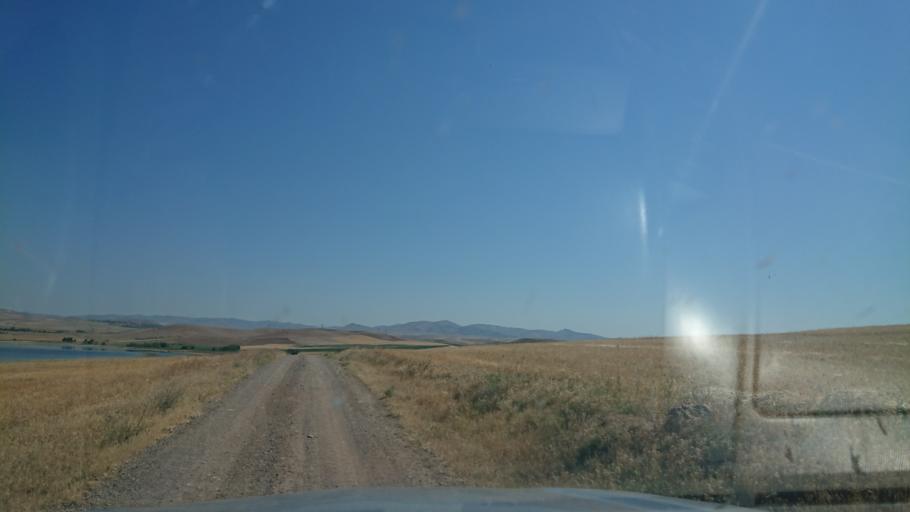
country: TR
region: Ankara
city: Evren
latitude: 39.0541
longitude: 33.8805
